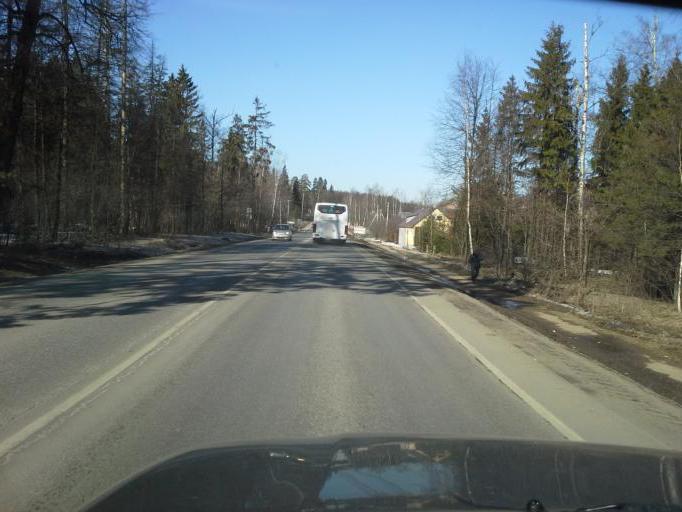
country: RU
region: Moskovskaya
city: Lesnoy Gorodok
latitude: 55.6657
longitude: 37.1776
